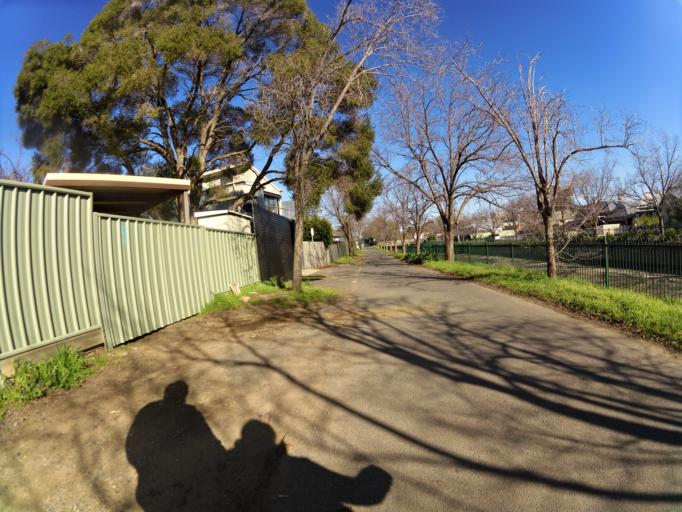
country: AU
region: Victoria
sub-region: Greater Bendigo
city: Bendigo
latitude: -36.7521
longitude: 144.2858
